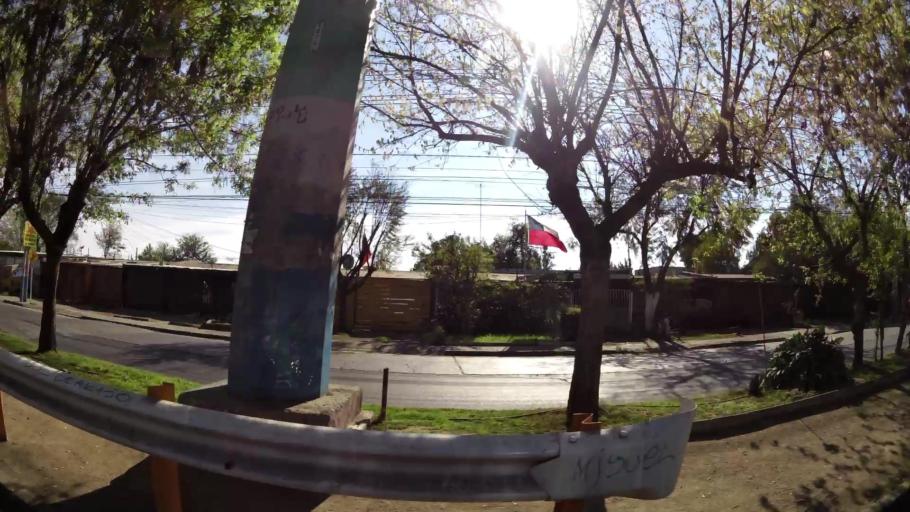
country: CL
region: Santiago Metropolitan
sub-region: Provincia de Santiago
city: Villa Presidente Frei, Nunoa, Santiago, Chile
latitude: -33.4673
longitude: -70.5674
